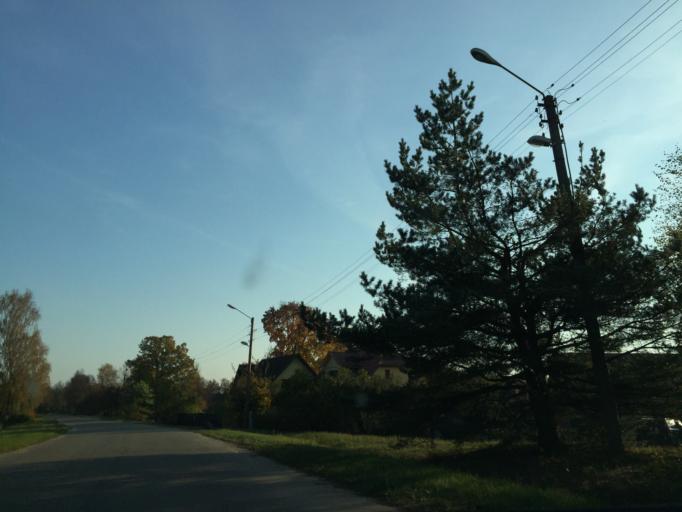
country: LV
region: Skrunda
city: Skrunda
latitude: 56.6791
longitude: 22.0124
